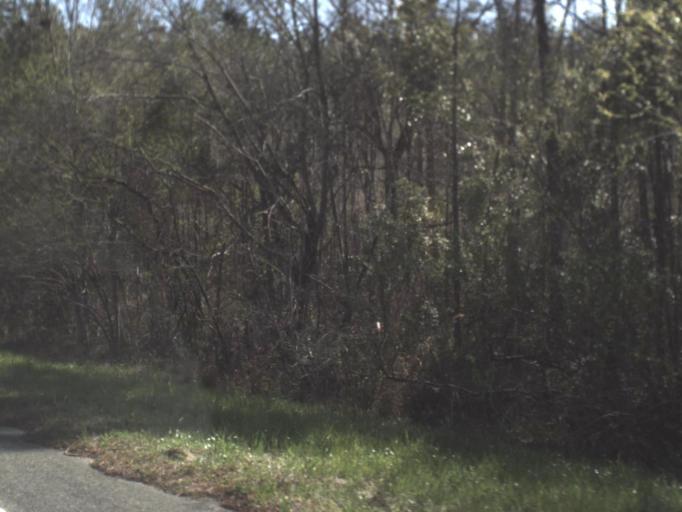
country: US
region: Florida
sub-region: Leon County
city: Woodville
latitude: 30.3233
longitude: -84.0342
